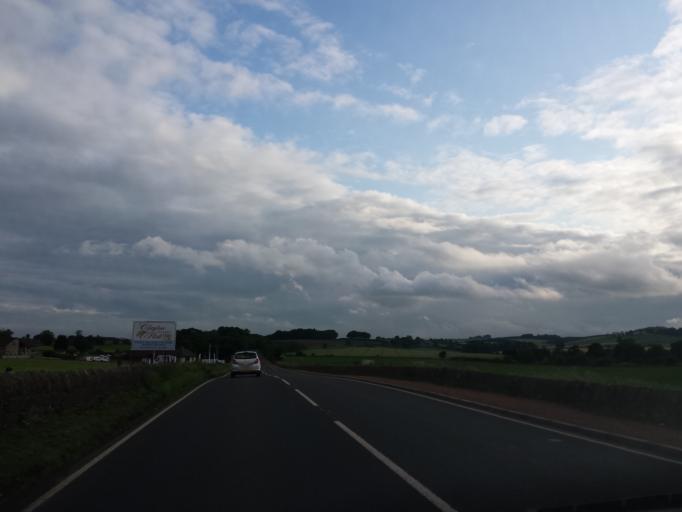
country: GB
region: Scotland
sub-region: Fife
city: Balmullo
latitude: 56.3558
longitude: -2.9228
